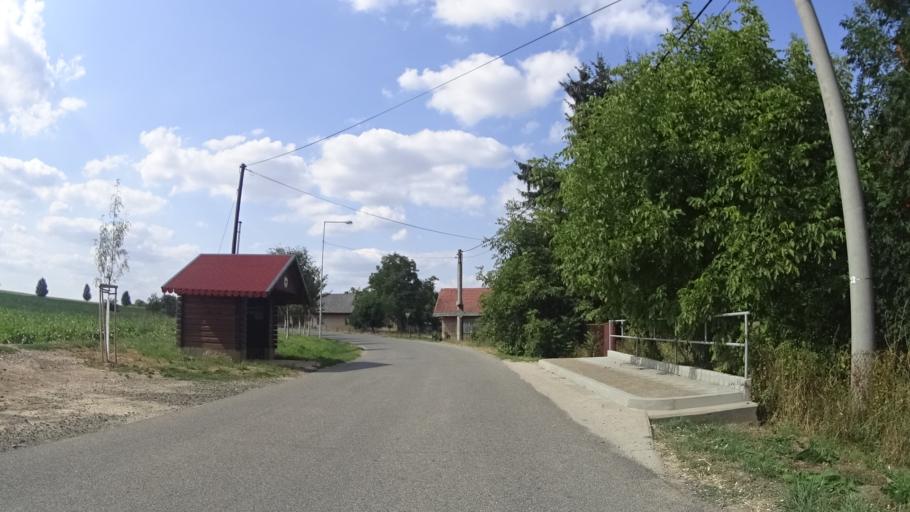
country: CZ
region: Kralovehradecky
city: Liban
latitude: 50.4072
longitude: 15.2693
